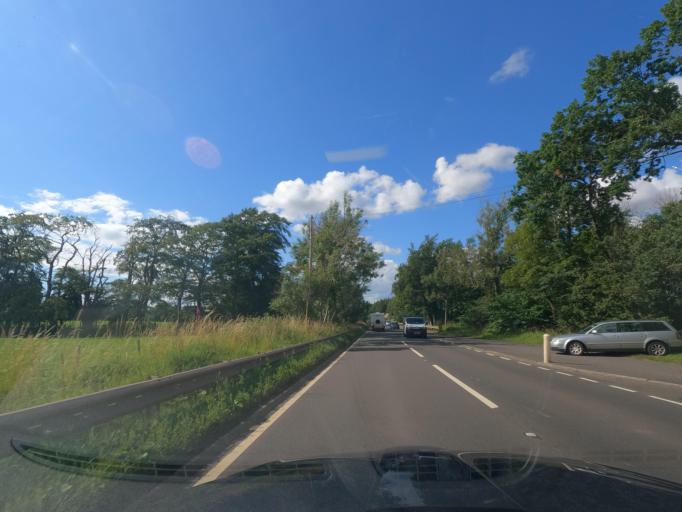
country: GB
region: Scotland
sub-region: East Lothian
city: Pencaitland
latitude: 55.8326
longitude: -2.8891
